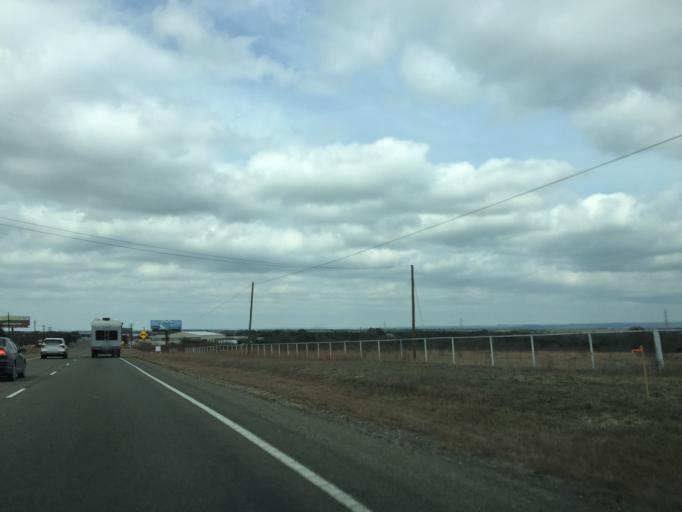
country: US
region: Texas
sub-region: Travis County
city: Briarcliff
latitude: 30.4558
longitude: -98.1522
